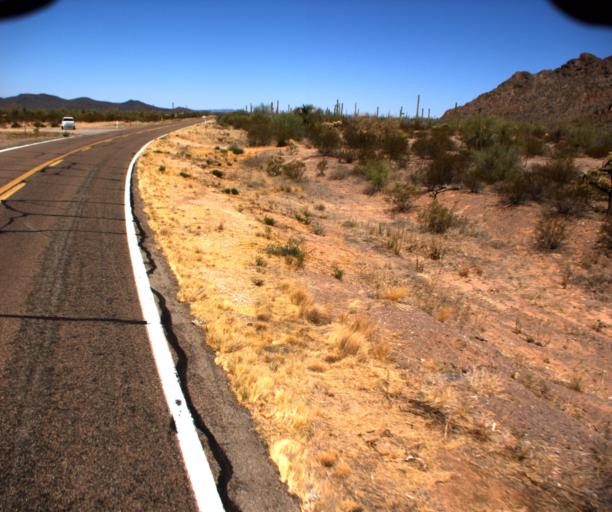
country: US
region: Arizona
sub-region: Pima County
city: Ajo
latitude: 32.2224
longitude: -112.6864
